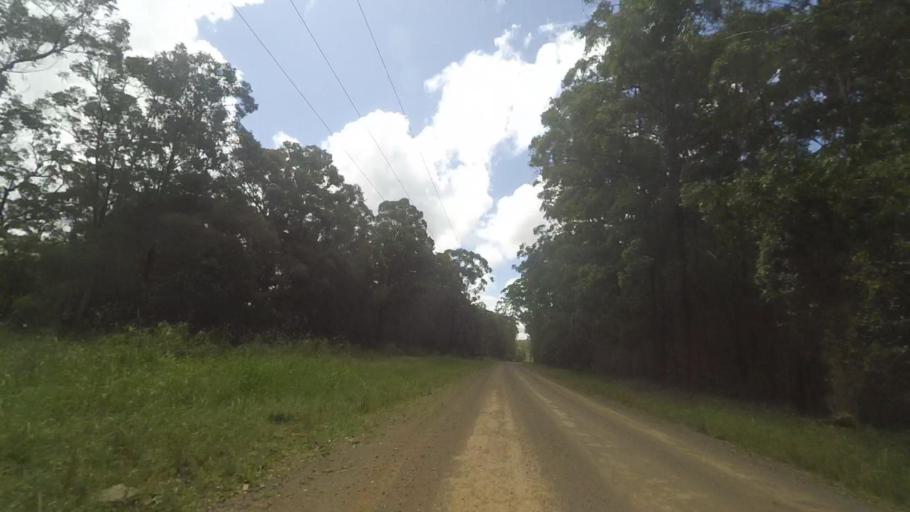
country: AU
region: New South Wales
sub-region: Great Lakes
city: Bulahdelah
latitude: -32.4955
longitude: 152.2774
